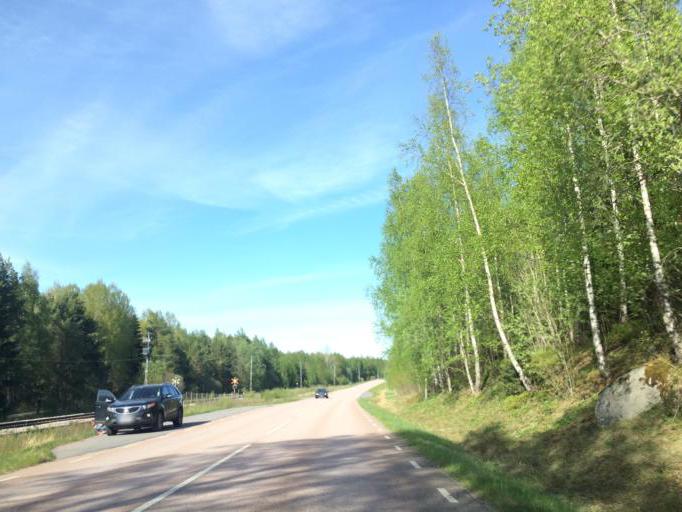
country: SE
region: Soedermanland
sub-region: Eskilstuna Kommun
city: Kvicksund
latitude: 59.4153
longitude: 16.2777
